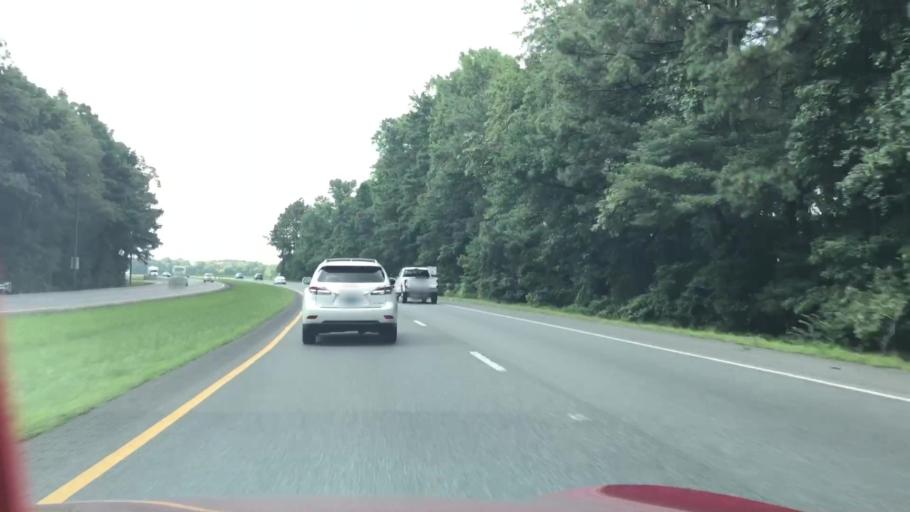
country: US
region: Maryland
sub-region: Worcester County
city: Pocomoke City
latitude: 38.0077
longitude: -75.5449
